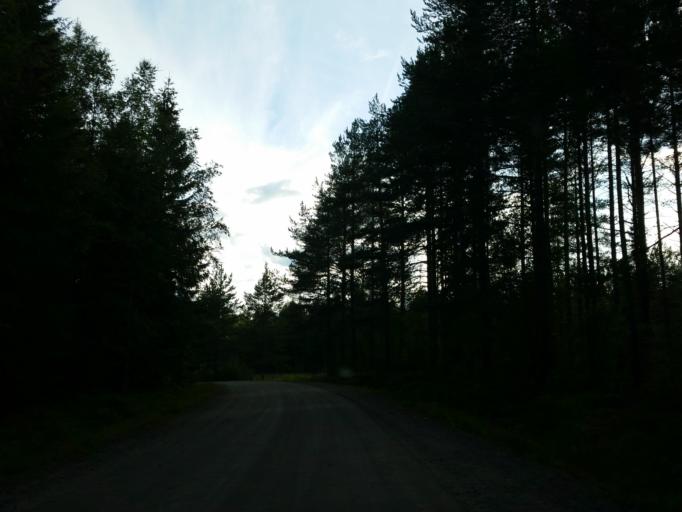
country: SE
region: Vaesterbotten
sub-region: Robertsfors Kommun
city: Robertsfors
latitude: 64.0443
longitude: 20.8496
